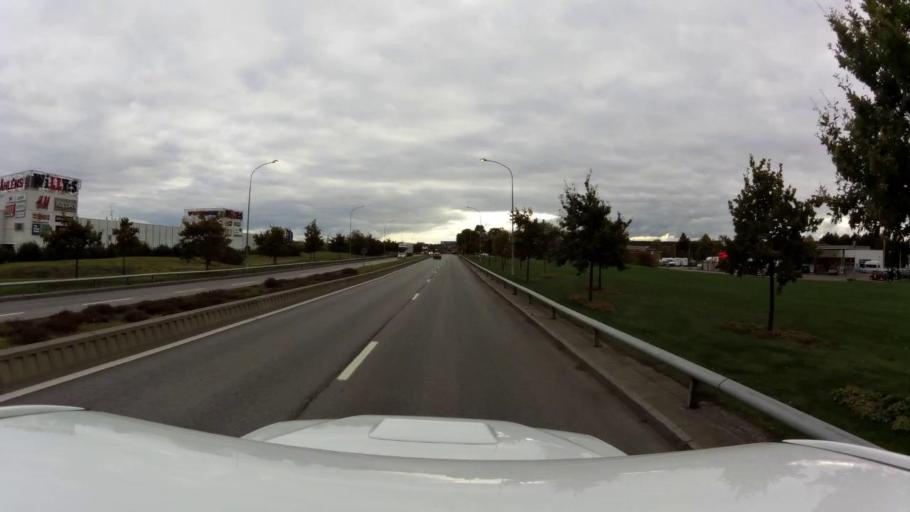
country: SE
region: OEstergoetland
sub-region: Linkopings Kommun
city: Linkoping
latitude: 58.4331
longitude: 15.5838
